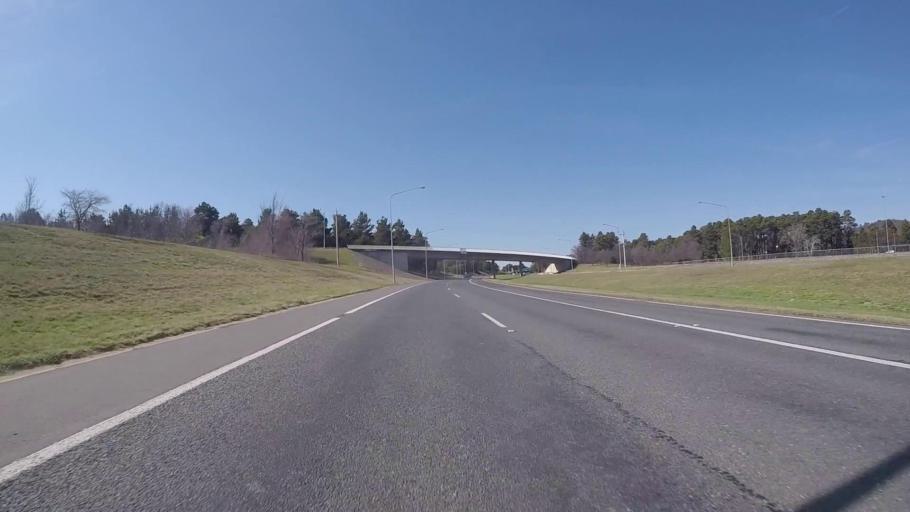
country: AU
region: Australian Capital Territory
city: Forrest
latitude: -35.3155
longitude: 149.0919
